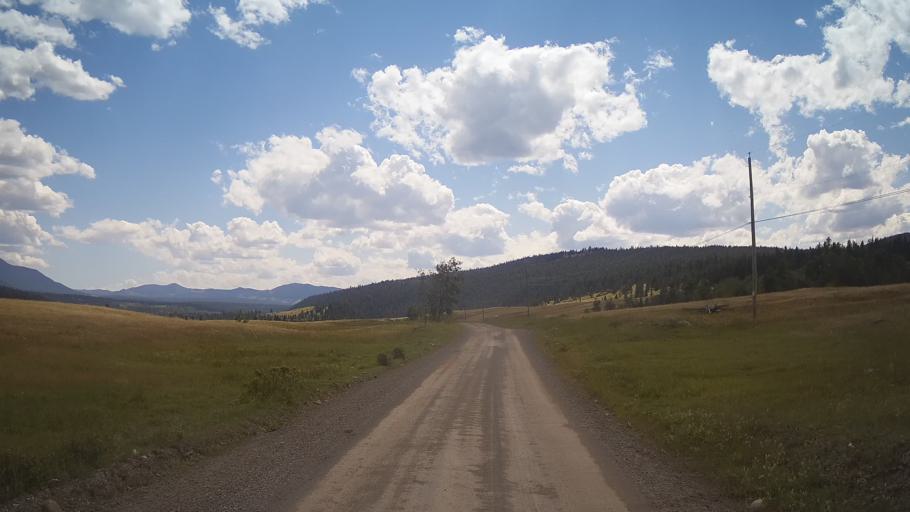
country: CA
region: British Columbia
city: Lillooet
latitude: 51.3152
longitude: -121.9829
